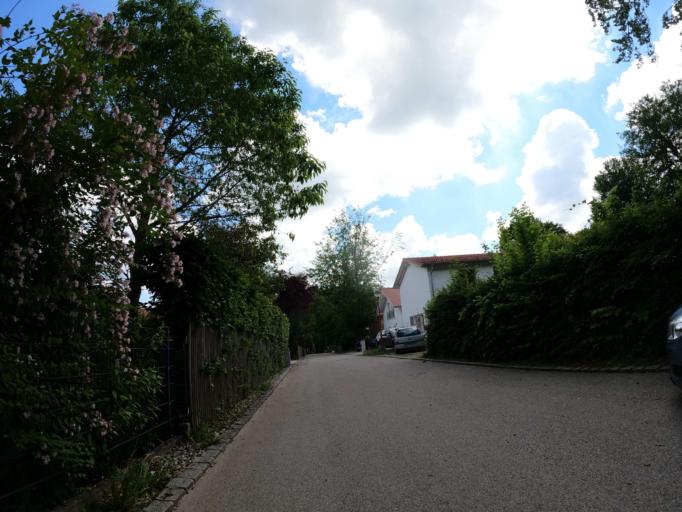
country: DE
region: Bavaria
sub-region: Upper Bavaria
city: Oberhaching
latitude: 47.9777
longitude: 11.5752
